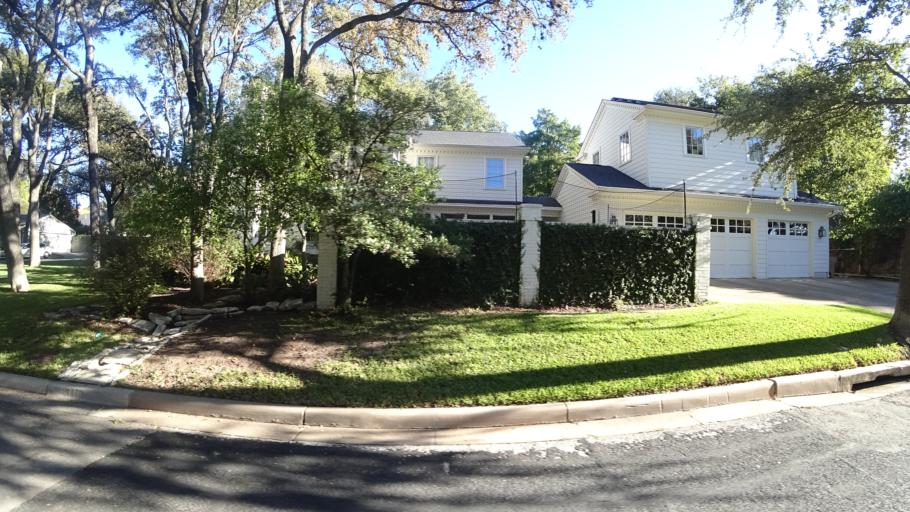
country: US
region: Texas
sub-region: Travis County
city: Rollingwood
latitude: 30.2947
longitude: -97.7716
